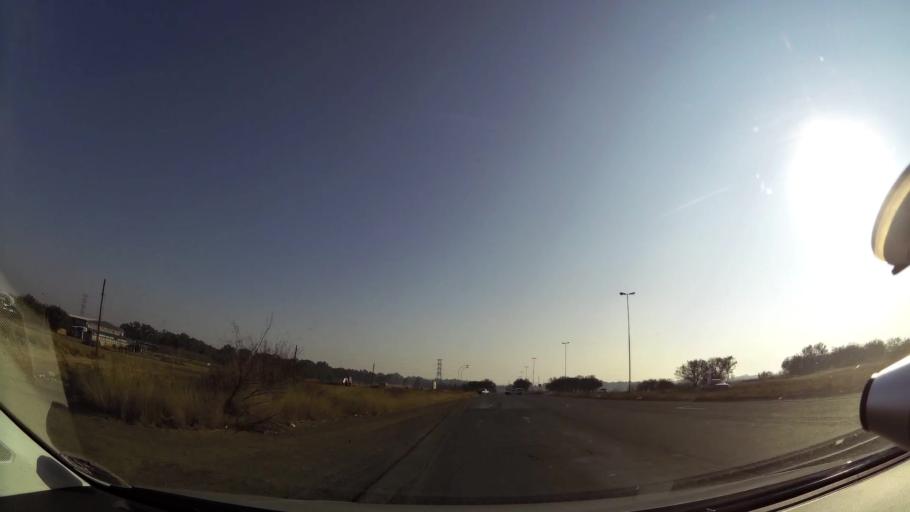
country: ZA
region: Orange Free State
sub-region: Mangaung Metropolitan Municipality
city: Bloemfontein
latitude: -29.1285
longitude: 26.2672
